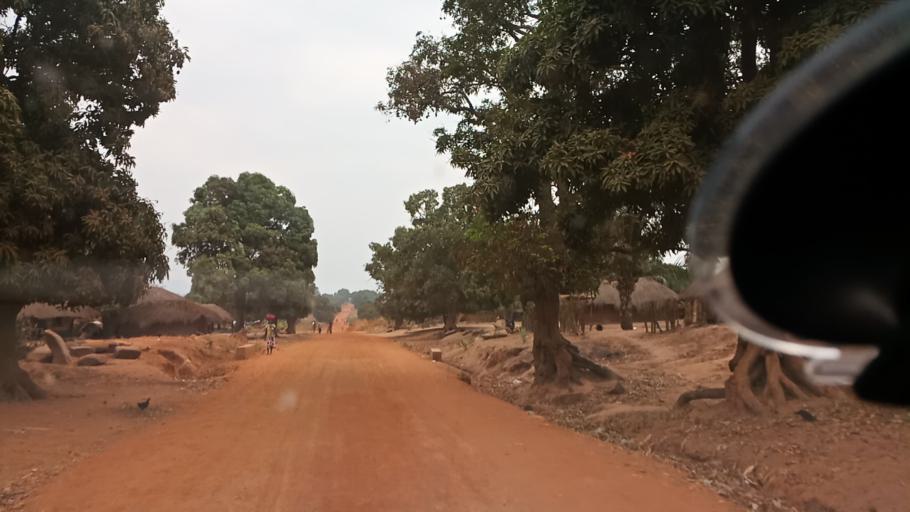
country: ZM
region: Luapula
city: Nchelenge
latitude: -9.1821
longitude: 28.2830
